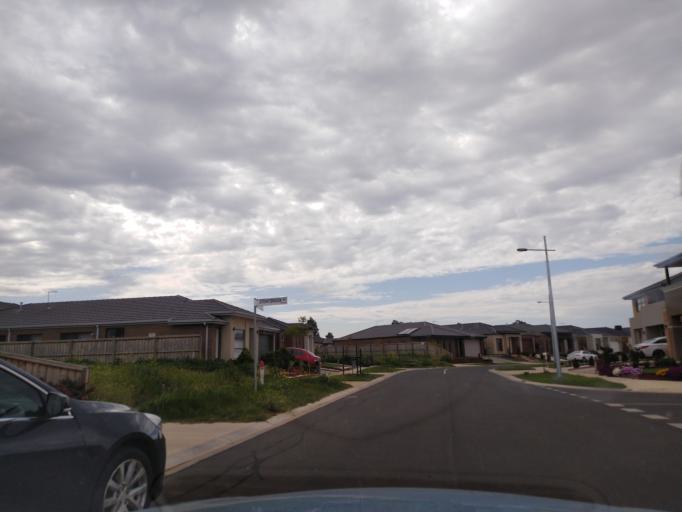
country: AU
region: Victoria
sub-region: Wyndham
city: Williams Landing
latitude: -37.8398
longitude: 144.7093
